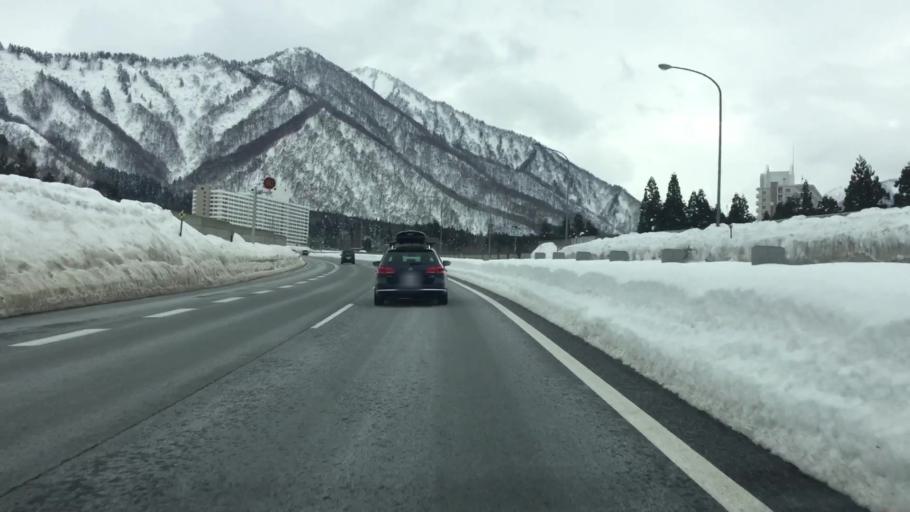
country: JP
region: Niigata
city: Shiozawa
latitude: 36.9083
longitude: 138.8422
